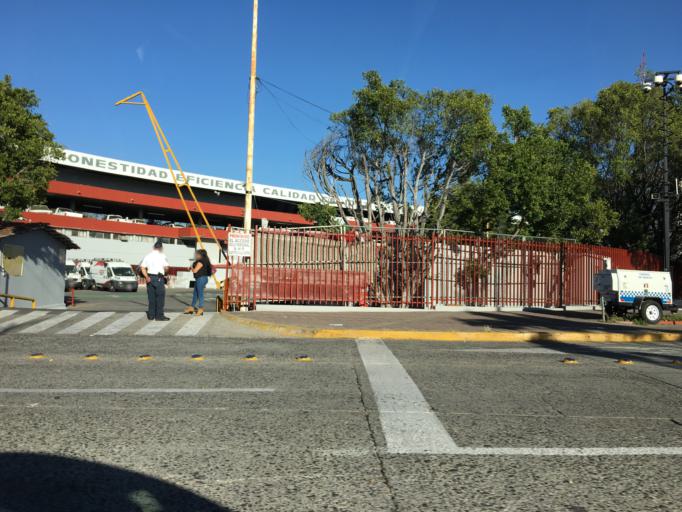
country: MX
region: Jalisco
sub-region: Zapopan
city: Zapopan
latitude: 20.7059
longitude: -103.3469
